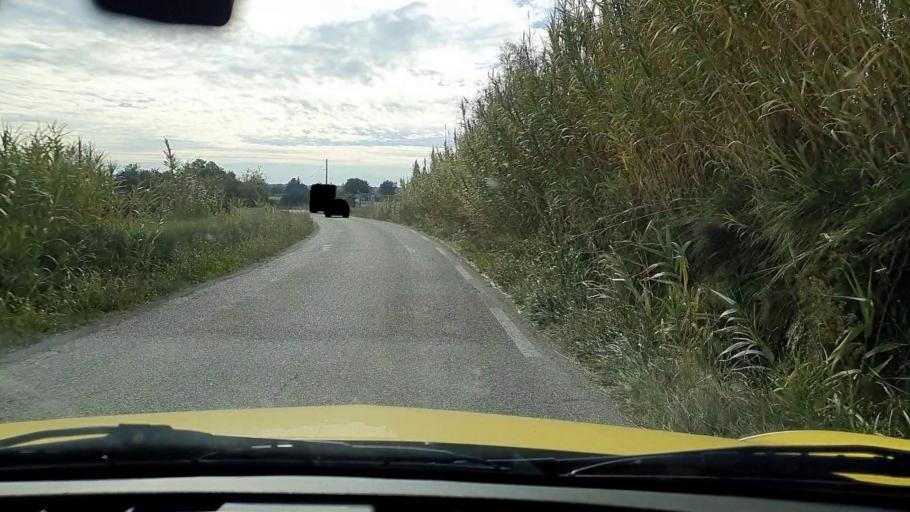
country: FR
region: Languedoc-Roussillon
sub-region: Departement du Gard
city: Jonquieres-Saint-Vincent
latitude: 43.8351
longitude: 4.5653
